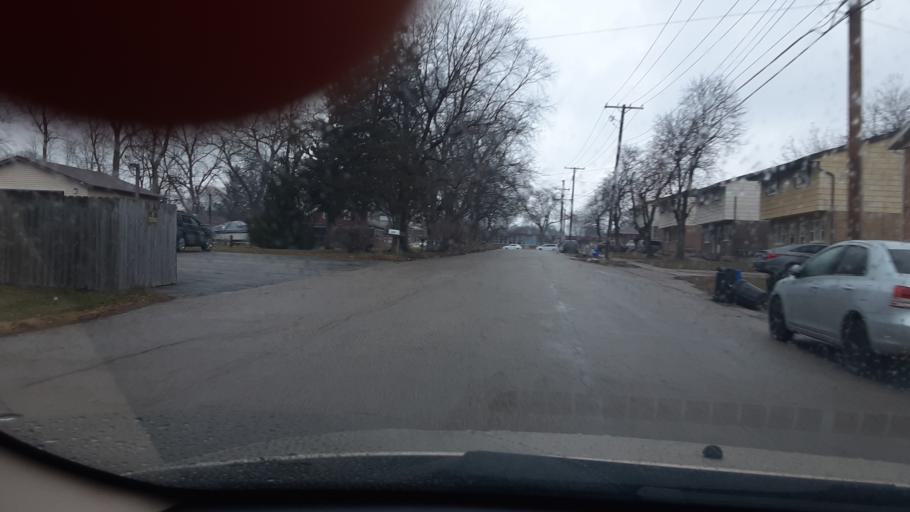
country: US
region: Illinois
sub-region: Winnebago County
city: Rockford
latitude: 42.3089
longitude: -89.1041
